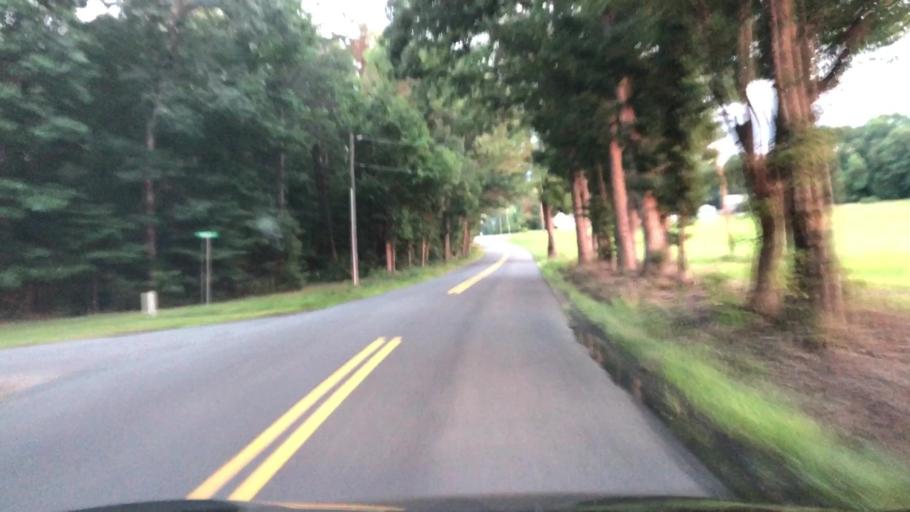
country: US
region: Virginia
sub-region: Stafford County
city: Falmouth
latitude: 38.4409
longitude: -77.5895
